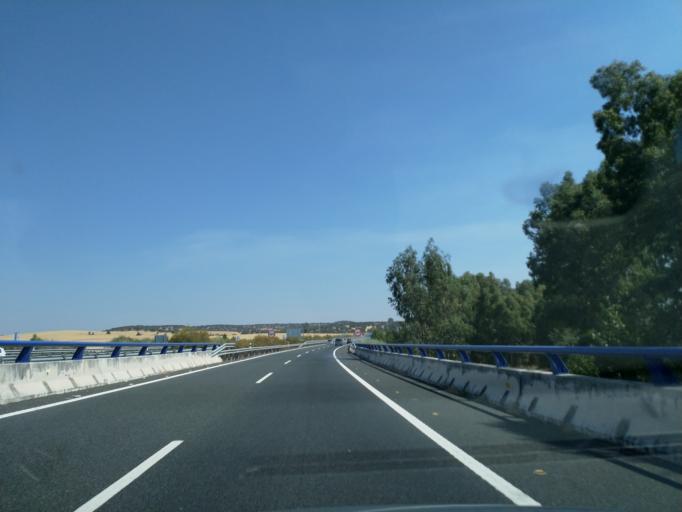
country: ES
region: Extremadura
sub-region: Provincia de Badajoz
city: Aljucen
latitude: 39.0469
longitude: -6.3376
